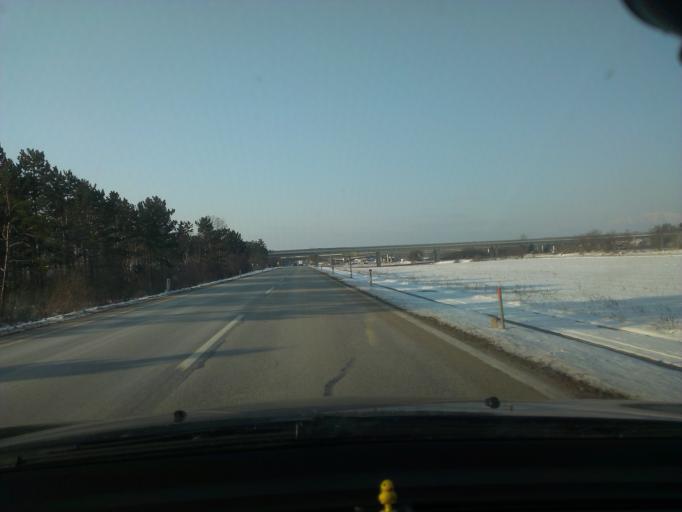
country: AT
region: Lower Austria
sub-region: Wiener Neustadt Stadt
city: Wiener Neustadt
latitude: 47.7907
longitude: 16.2100
